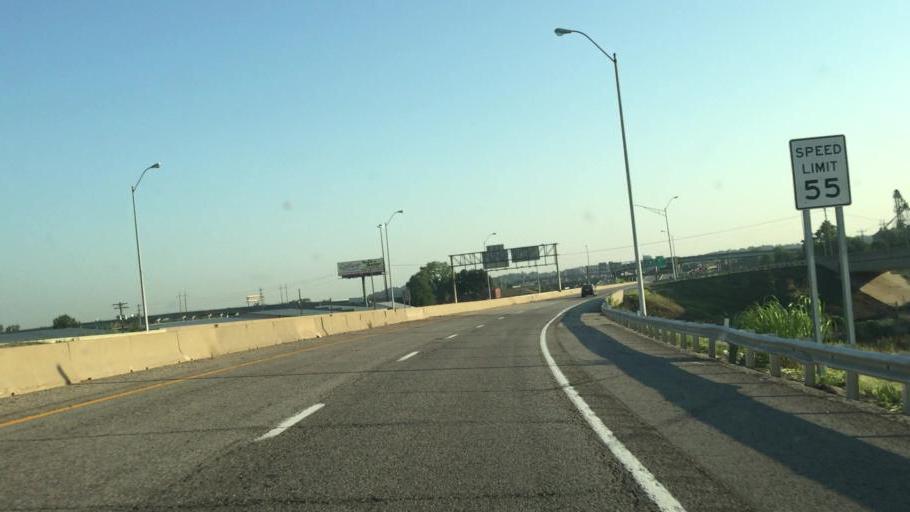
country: US
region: Kansas
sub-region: Doniphan County
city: Elwood
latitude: 39.7426
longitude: -94.8534
